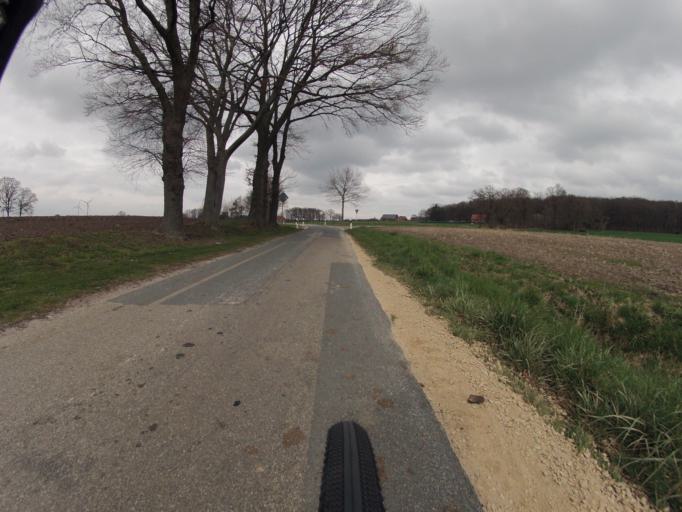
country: DE
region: North Rhine-Westphalia
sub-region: Regierungsbezirk Munster
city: Mettingen
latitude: 52.3262
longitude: 7.8225
